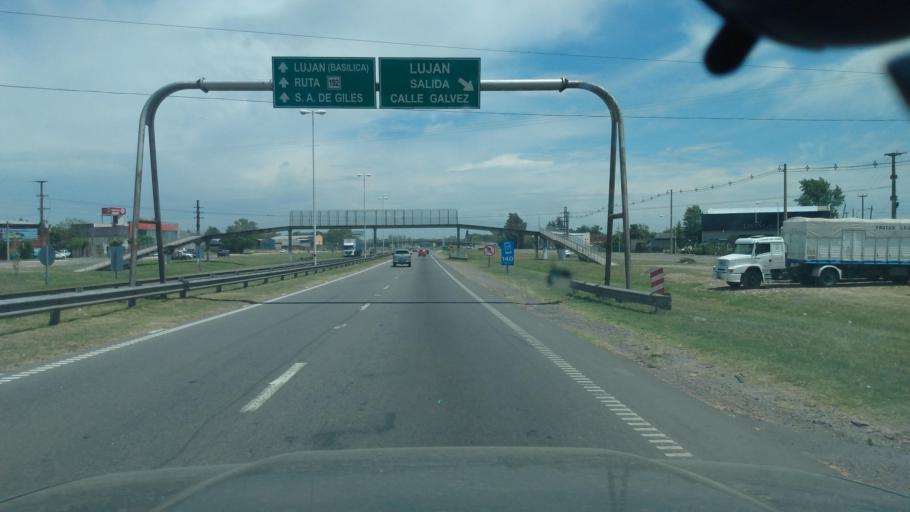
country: AR
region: Buenos Aires
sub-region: Partido de Lujan
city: Lujan
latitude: -34.5547
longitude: -59.1027
